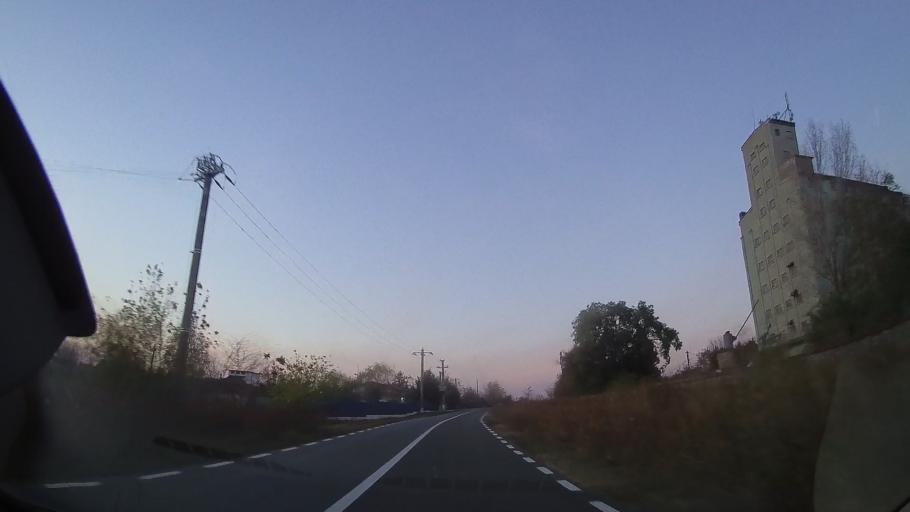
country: RO
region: Constanta
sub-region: Comuna Cobadin
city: Cobadin
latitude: 44.0515
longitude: 28.2480
